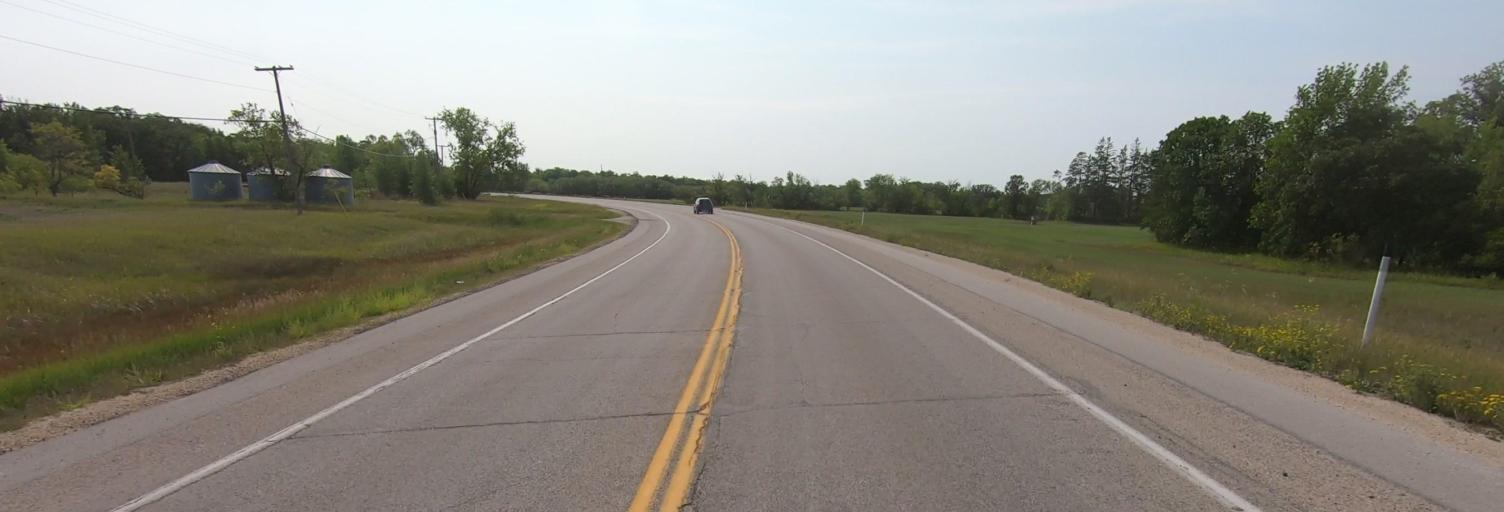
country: CA
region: Manitoba
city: Winnipeg
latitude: 49.7413
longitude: -97.1227
